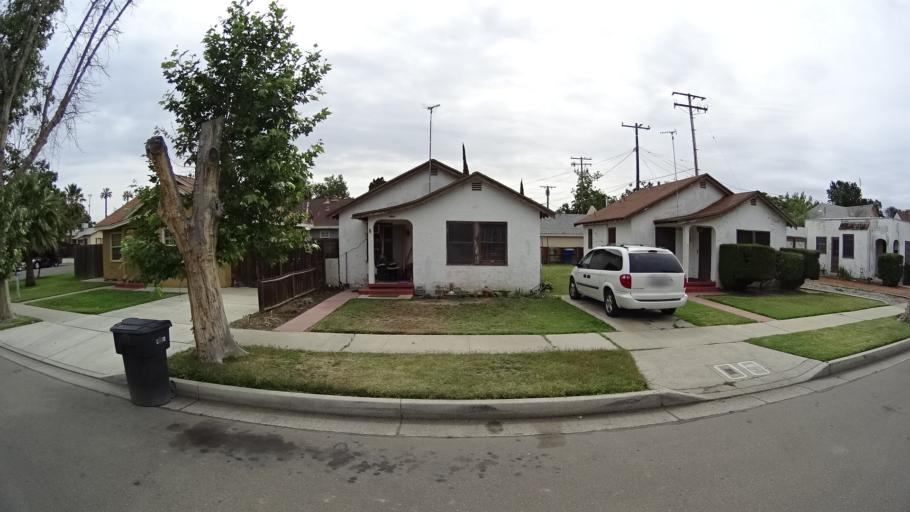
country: US
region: California
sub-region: Kings County
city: Hanford
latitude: 36.3354
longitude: -119.6477
